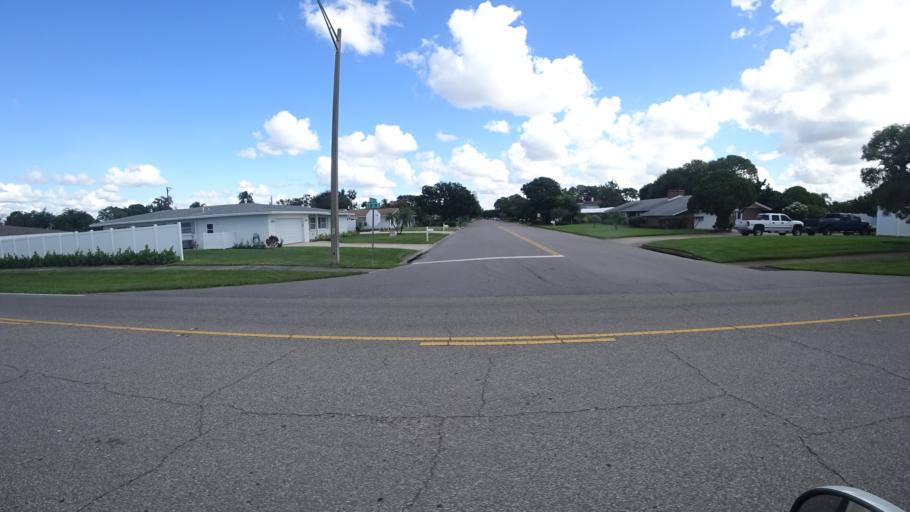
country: US
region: Florida
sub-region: Manatee County
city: West Bradenton
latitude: 27.4911
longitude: -82.6204
